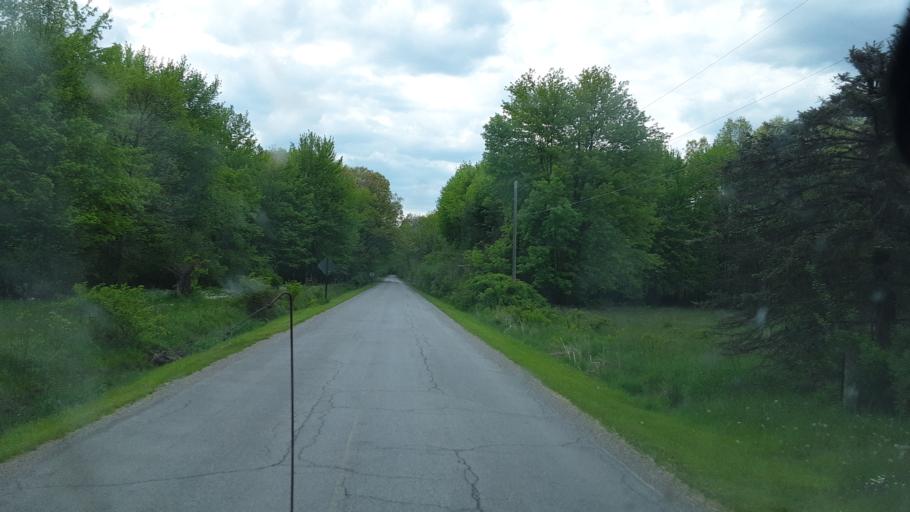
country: US
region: Ohio
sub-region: Portage County
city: Windham
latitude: 41.2709
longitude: -80.9782
